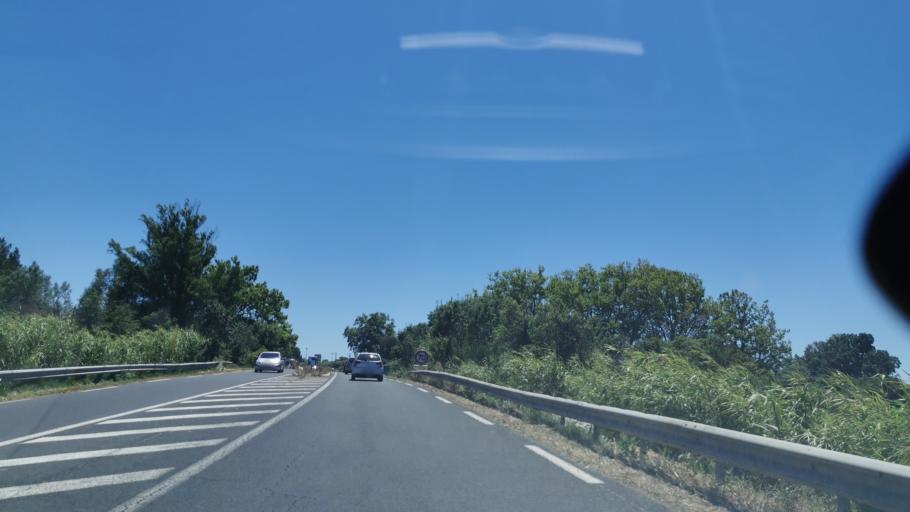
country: FR
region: Languedoc-Roussillon
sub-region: Departement de l'Herault
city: Beziers
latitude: 43.3314
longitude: 3.1942
